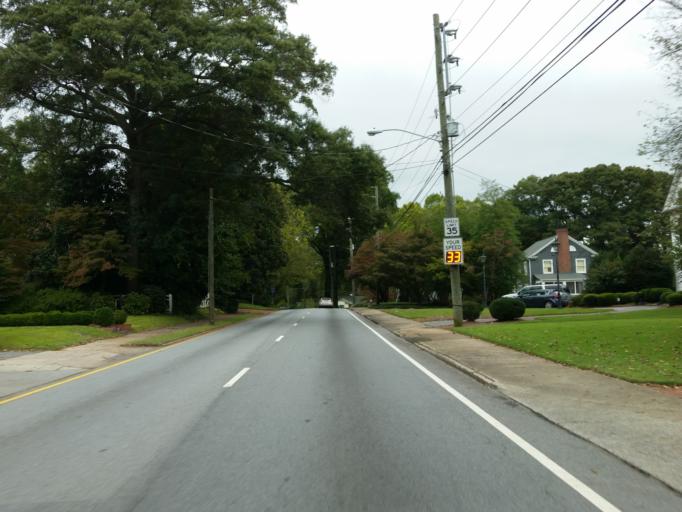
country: US
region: Georgia
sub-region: Cobb County
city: Marietta
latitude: 33.9620
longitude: -84.5482
